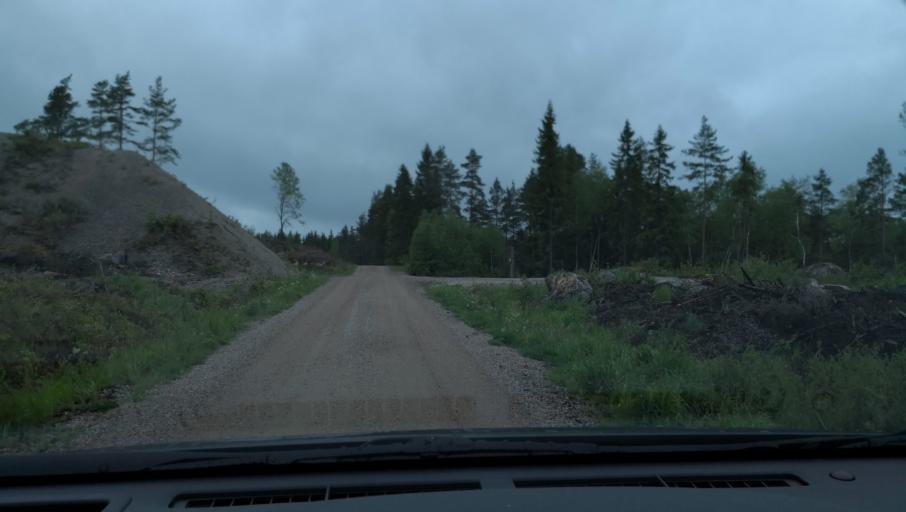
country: SE
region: Uppsala
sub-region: Enkopings Kommun
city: Orsundsbro
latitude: 59.9413
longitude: 17.3116
